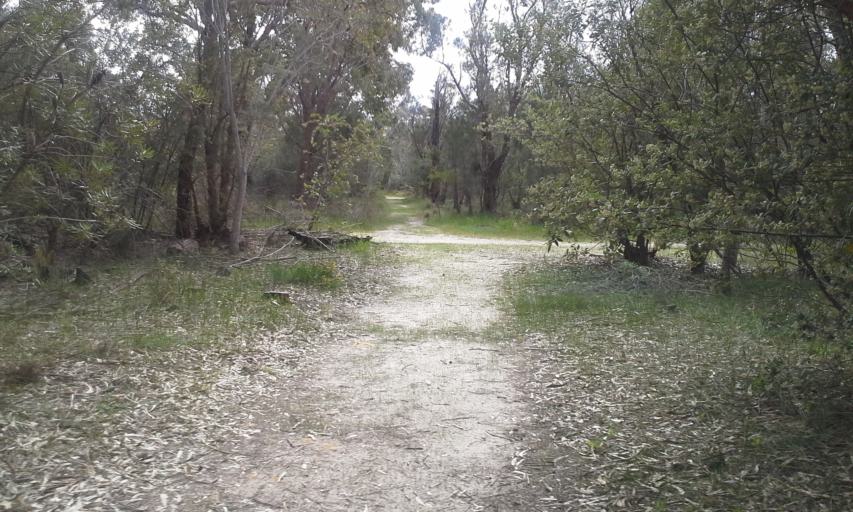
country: AU
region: Western Australia
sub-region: City of Perth
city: West Perth
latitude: -31.9590
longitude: 115.8347
